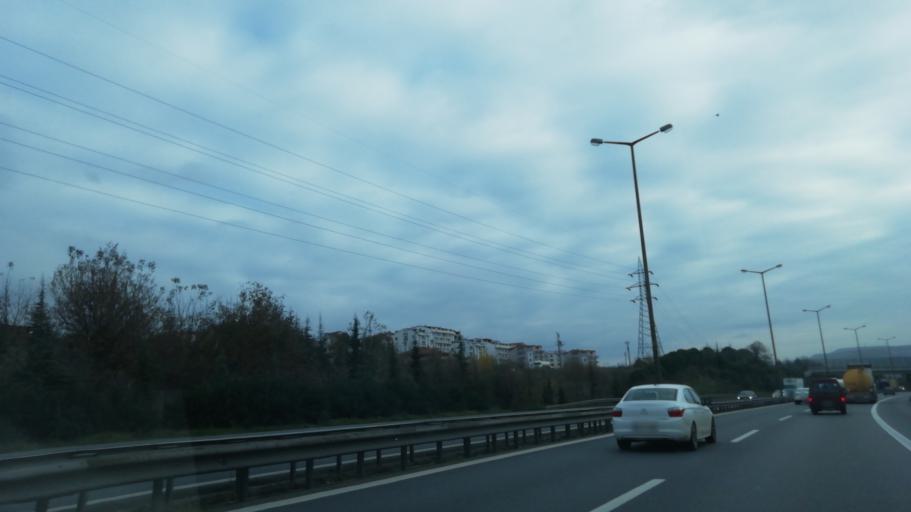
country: TR
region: Kocaeli
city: Izmit
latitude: 40.7860
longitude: 29.9512
